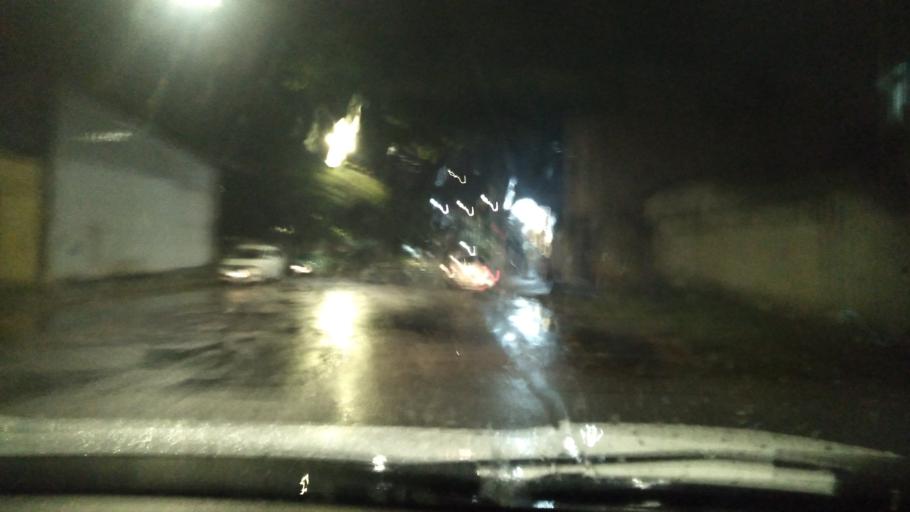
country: BR
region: Minas Gerais
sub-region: Belo Horizonte
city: Belo Horizonte
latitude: -19.8975
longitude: -43.9583
